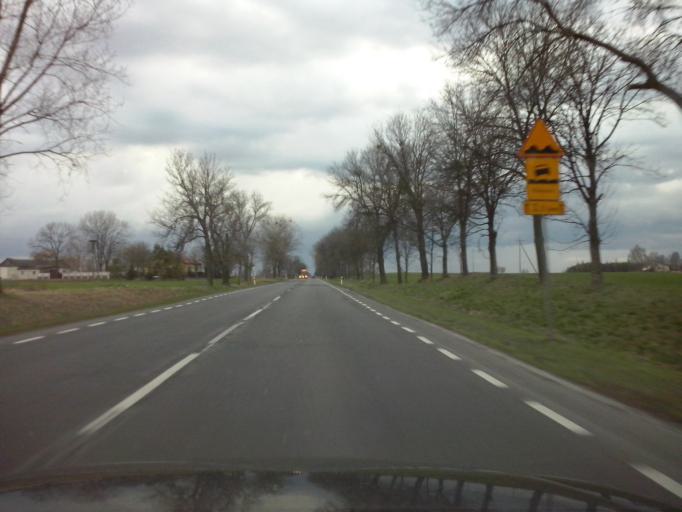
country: PL
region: Lublin Voivodeship
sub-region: Powiat chelmski
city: Rejowiec
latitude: 51.1695
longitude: 23.3285
